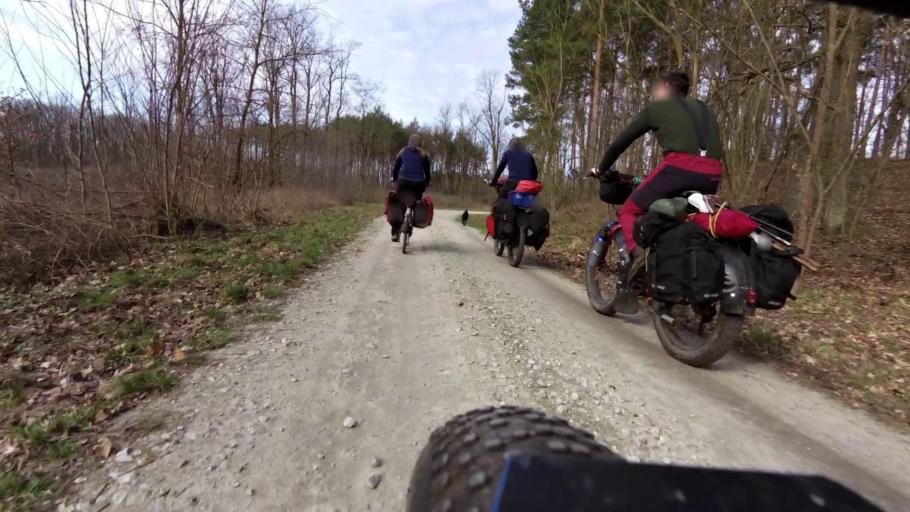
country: DE
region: Brandenburg
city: Brieskow-Finkenheerd
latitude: 52.2861
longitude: 14.6353
